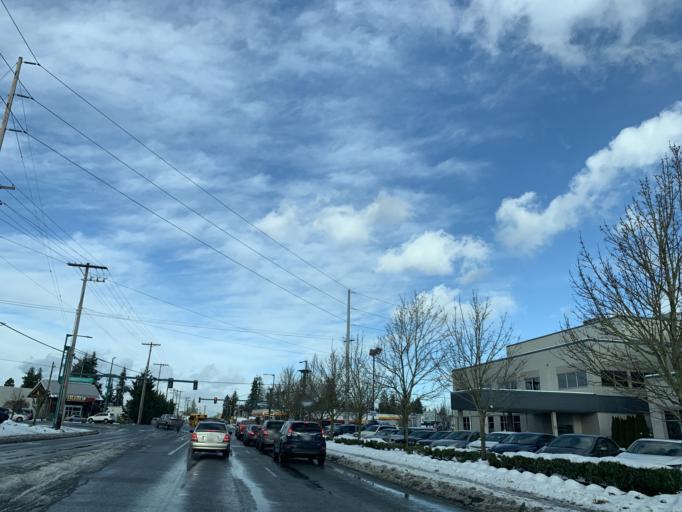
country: US
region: Washington
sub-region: Snohomish County
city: Martha Lake
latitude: 47.9045
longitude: -122.2389
